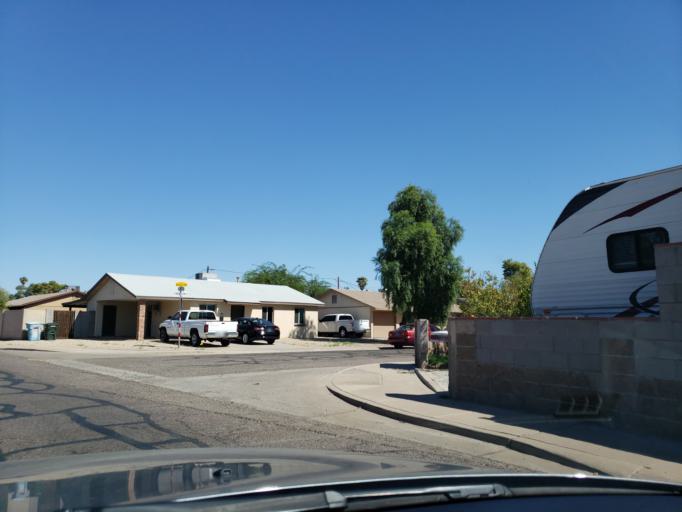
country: US
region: Arizona
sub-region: Maricopa County
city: Tolleson
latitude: 33.4902
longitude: -112.2305
